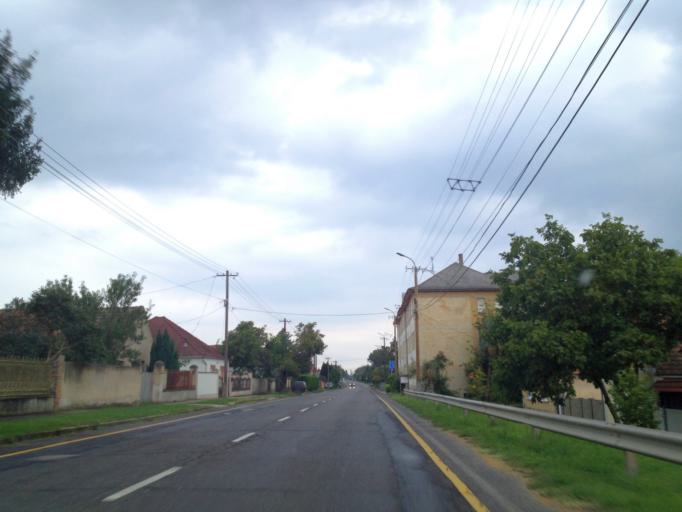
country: AT
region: Burgenland
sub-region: Politischer Bezirk Neusiedl am See
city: Nickelsdorf
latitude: 47.9163
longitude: 17.1491
